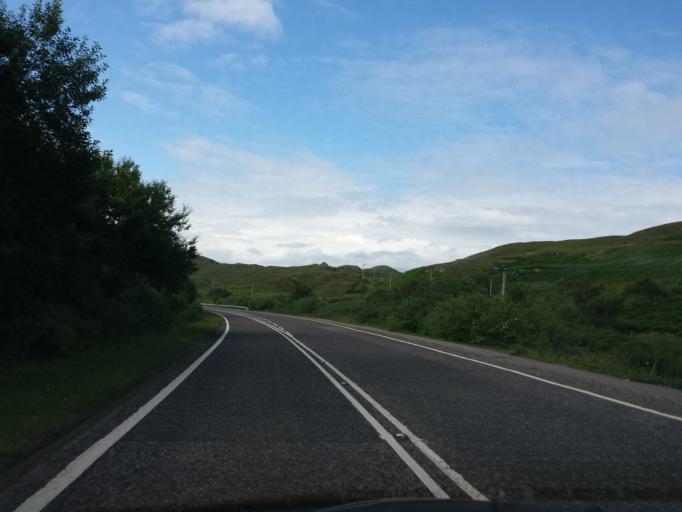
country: GB
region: Scotland
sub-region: Argyll and Bute
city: Isle Of Mull
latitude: 56.9873
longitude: -5.8253
